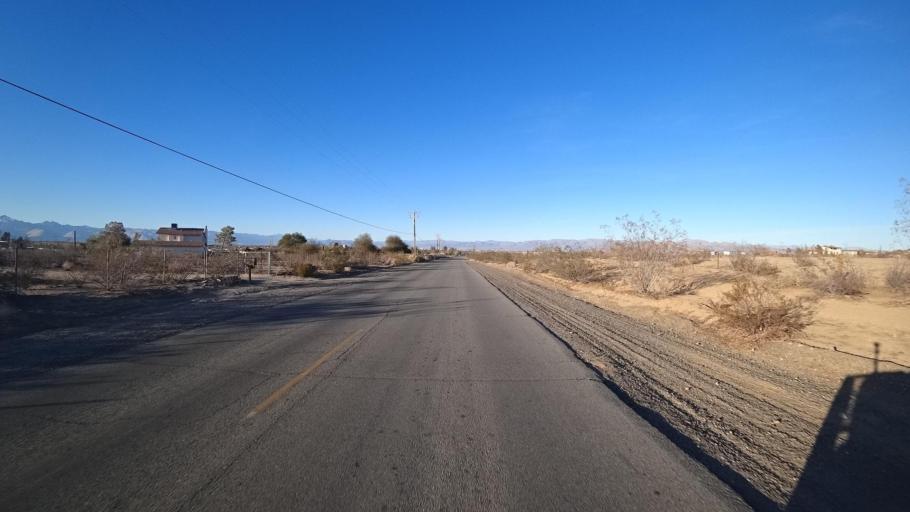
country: US
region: California
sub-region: Kern County
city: Ridgecrest
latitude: 35.5897
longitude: -117.6528
